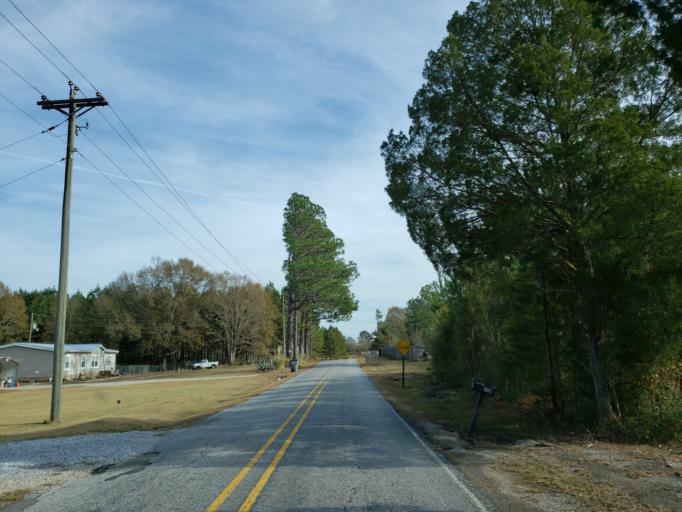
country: US
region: Mississippi
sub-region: Forrest County
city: Rawls Springs
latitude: 31.4132
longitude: -89.4134
